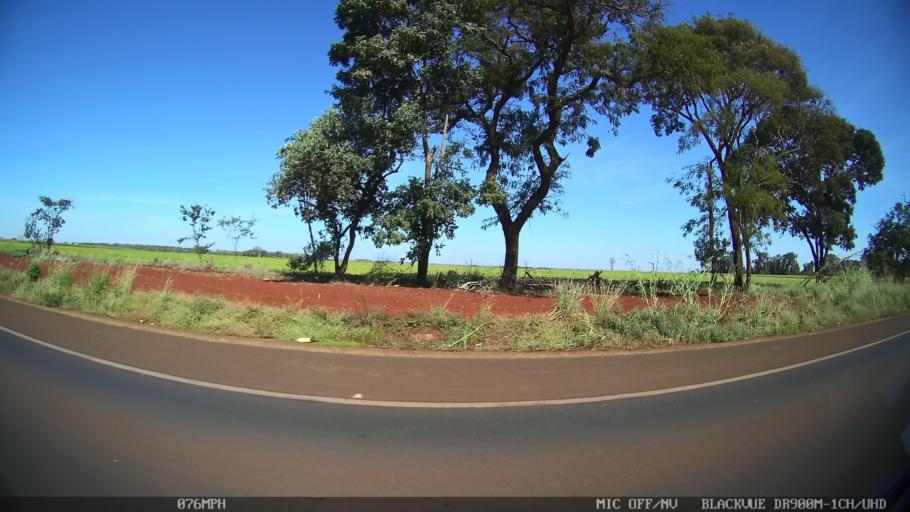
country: BR
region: Sao Paulo
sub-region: Guaira
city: Guaira
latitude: -20.4447
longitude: -48.3770
